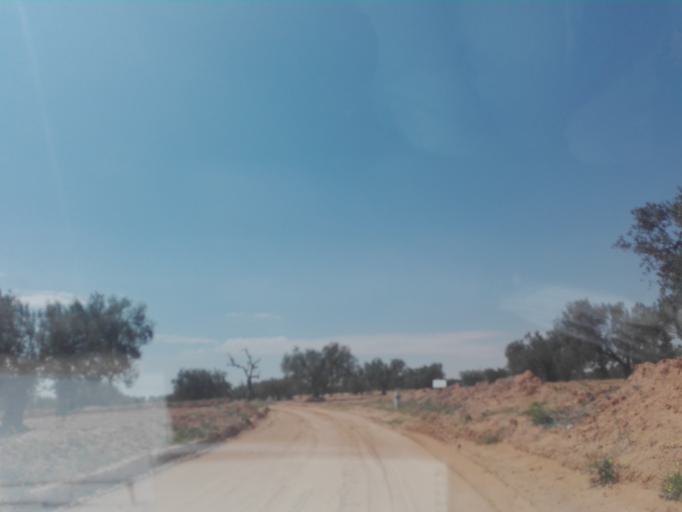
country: TN
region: Safaqis
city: Bi'r `Ali Bin Khalifah
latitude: 34.6082
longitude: 10.3529
